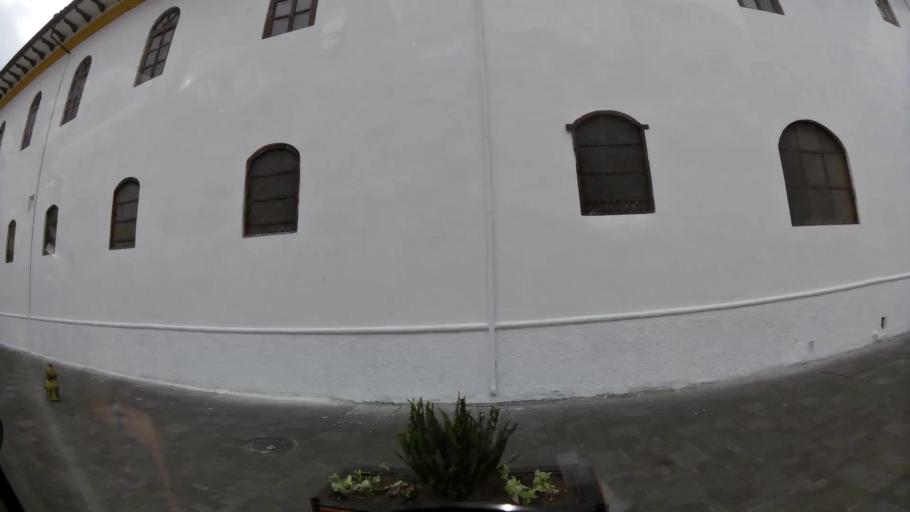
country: EC
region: Azuay
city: Cuenca
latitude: -2.9029
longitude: -79.0021
